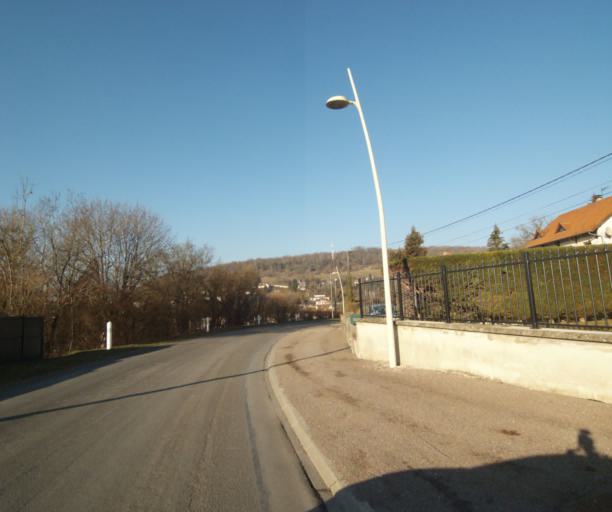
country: FR
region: Champagne-Ardenne
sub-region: Departement de la Haute-Marne
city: Chevillon
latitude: 48.5218
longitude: 5.1167
